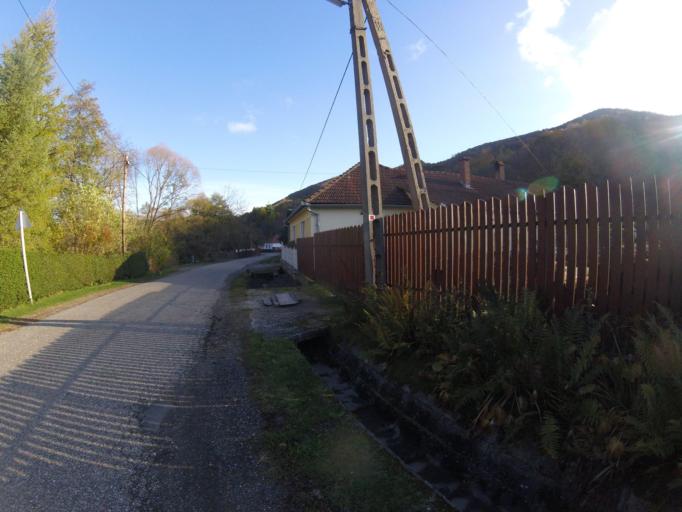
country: HU
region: Borsod-Abauj-Zemplen
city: Tolcsva
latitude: 48.3792
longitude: 21.3942
